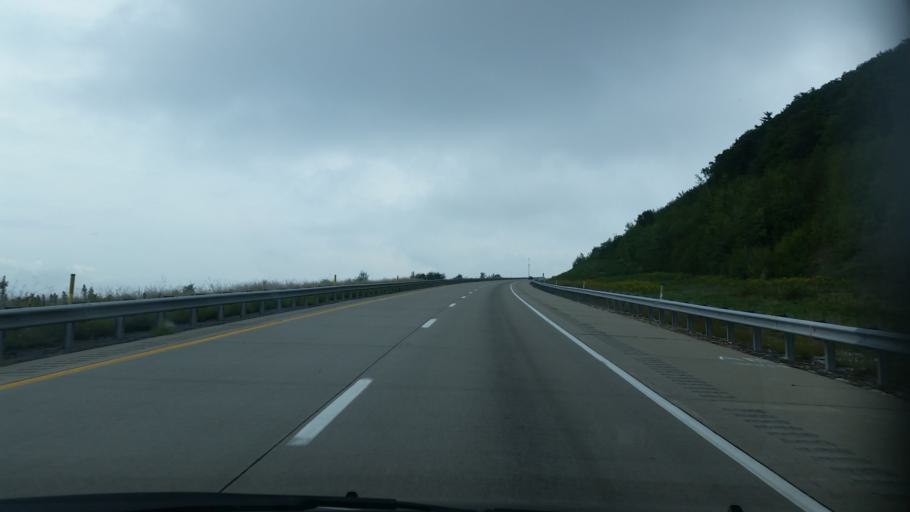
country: US
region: Pennsylvania
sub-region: Centre County
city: Stormstown
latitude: 40.8282
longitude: -77.9919
